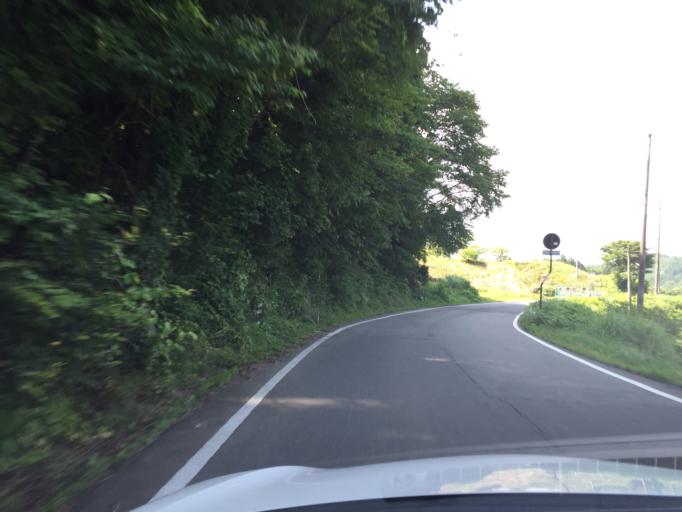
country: JP
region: Ibaraki
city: Kitaibaraki
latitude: 36.9714
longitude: 140.7037
